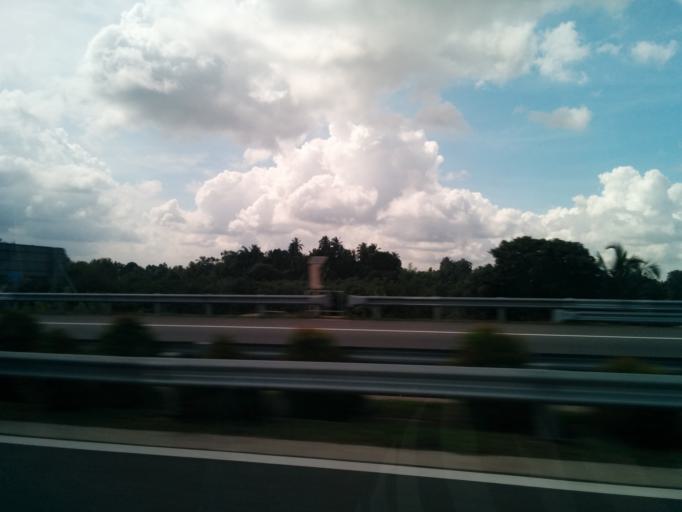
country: LK
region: Western
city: Wattala
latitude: 6.9902
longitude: 79.9018
